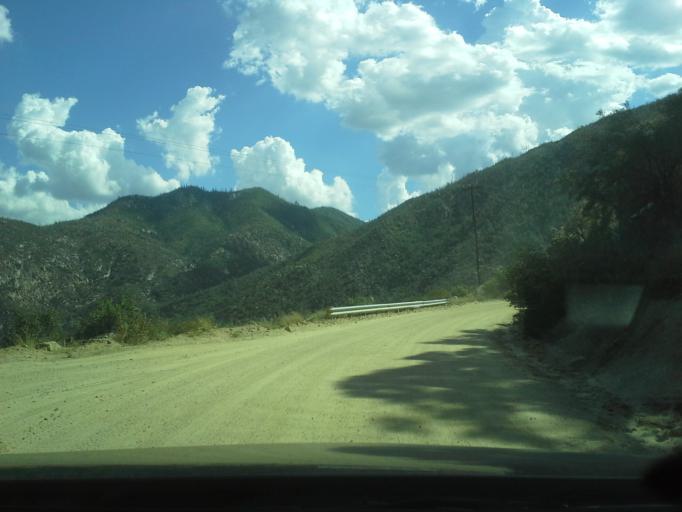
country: US
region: Arizona
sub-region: Yavapai County
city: Mayer
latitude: 34.2146
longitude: -112.3248
